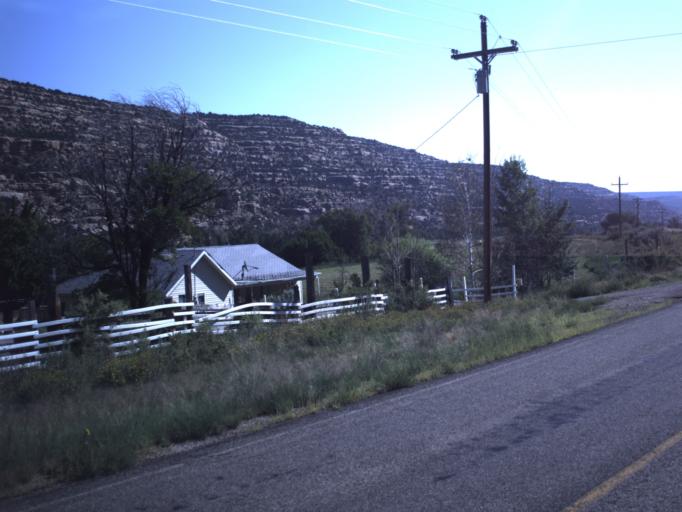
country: US
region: Utah
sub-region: Duchesne County
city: Duchesne
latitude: 40.2959
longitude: -110.5919
